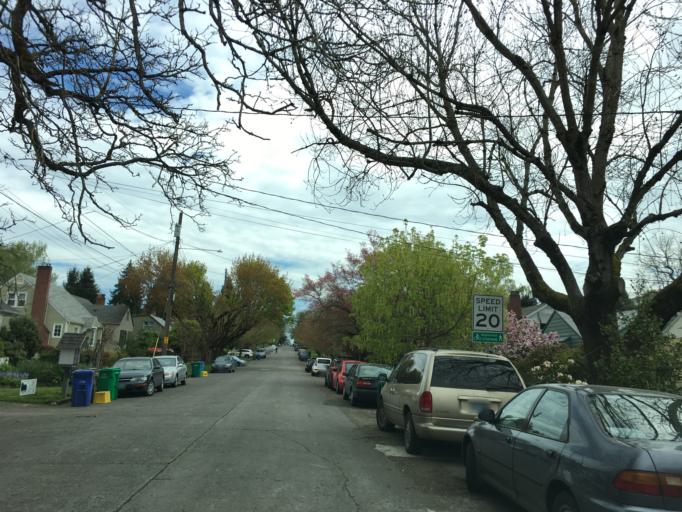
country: US
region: Oregon
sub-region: Multnomah County
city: Lents
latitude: 45.5242
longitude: -122.6021
